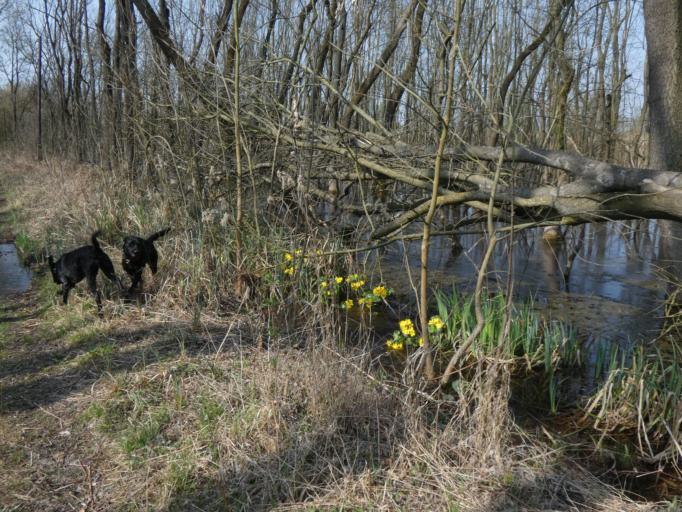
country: HU
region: Pest
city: Ocsa
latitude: 47.2564
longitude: 19.2341
